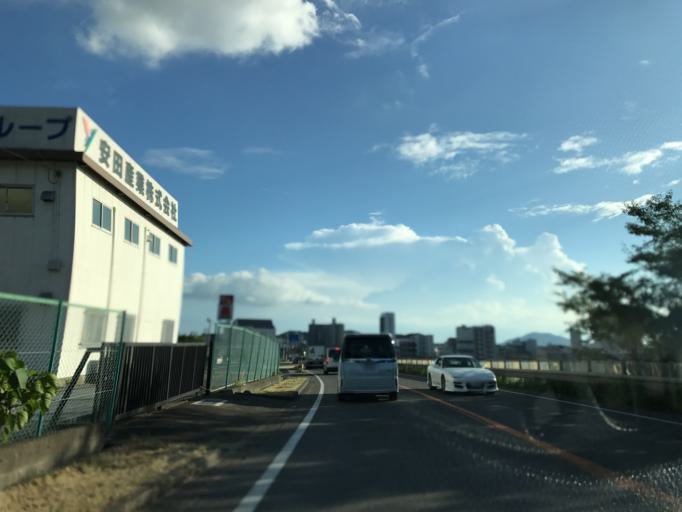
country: JP
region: Shiga Prefecture
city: Hikone
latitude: 35.2745
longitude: 136.2686
